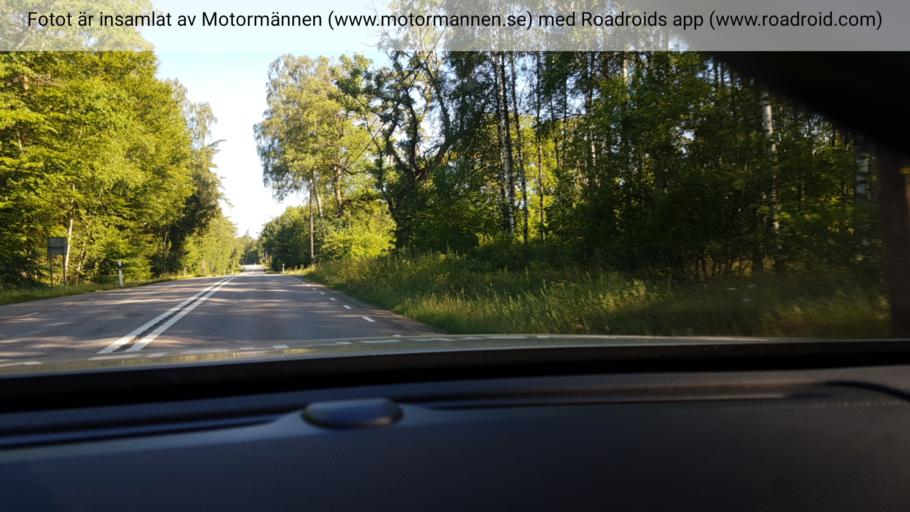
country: SE
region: Kronoberg
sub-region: Markaryds Kommun
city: Markaryd
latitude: 56.4073
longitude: 13.6432
